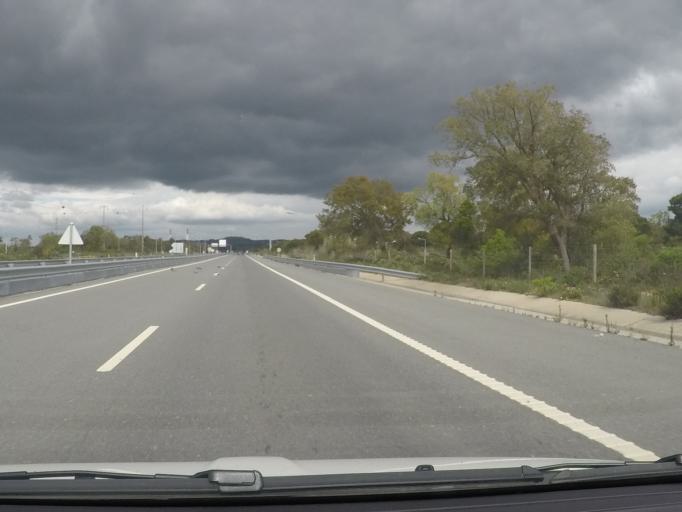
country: PT
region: Setubal
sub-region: Santiago do Cacem
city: Santo Andre
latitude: 37.9964
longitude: -8.7566
